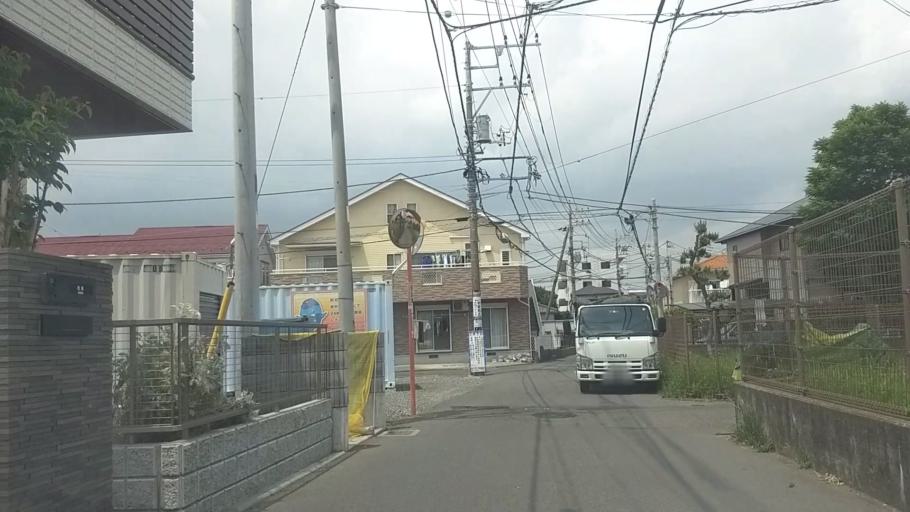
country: JP
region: Kanagawa
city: Chigasaki
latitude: 35.3552
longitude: 139.3980
